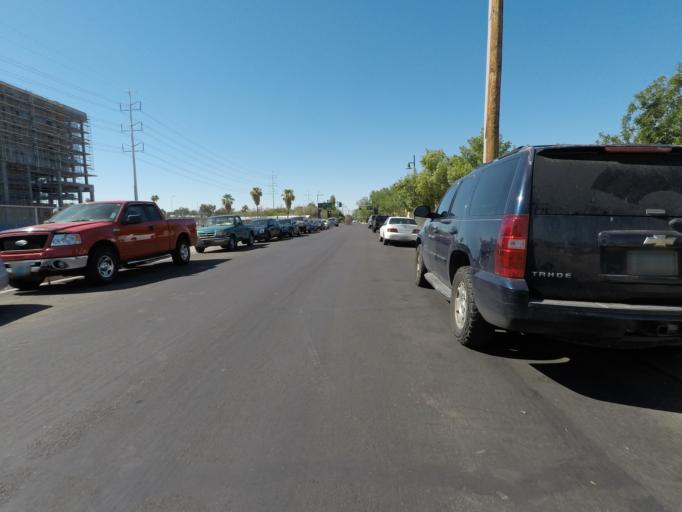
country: US
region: Arizona
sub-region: Maricopa County
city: Tempe Junction
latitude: 33.4230
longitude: -111.9443
